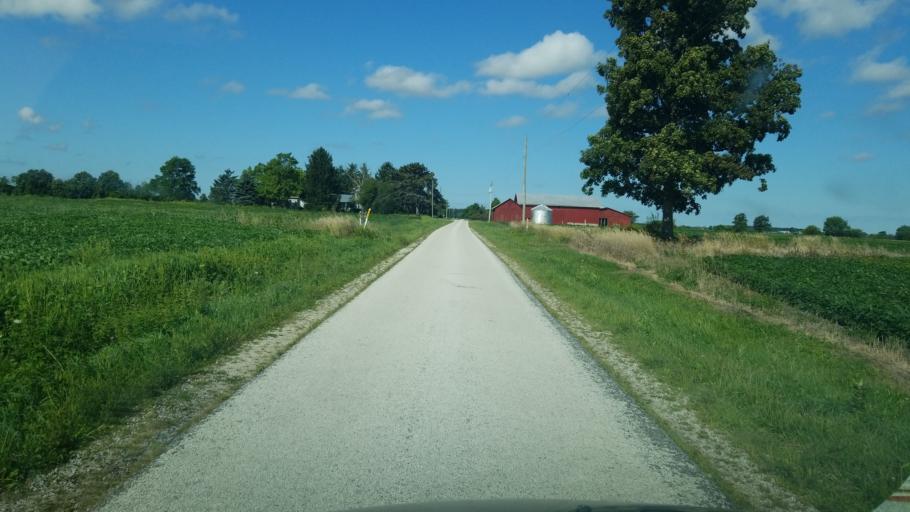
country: US
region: Ohio
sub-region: Seneca County
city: Fostoria
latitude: 41.0648
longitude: -83.4245
